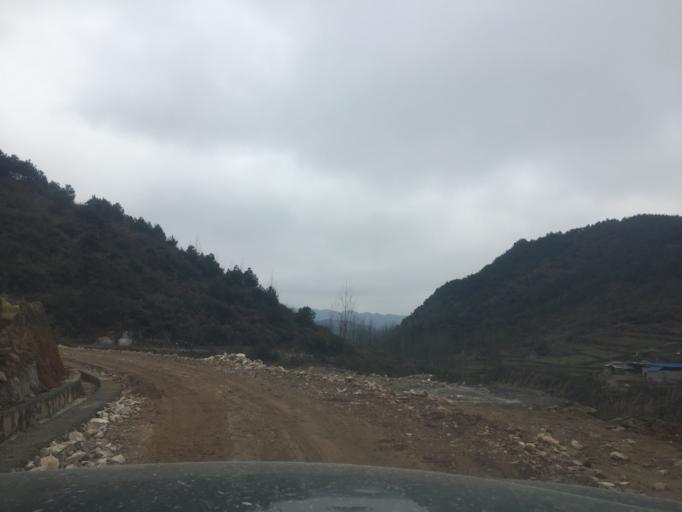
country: CN
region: Guizhou Sheng
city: Jiancha
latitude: 28.1765
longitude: 108.0014
